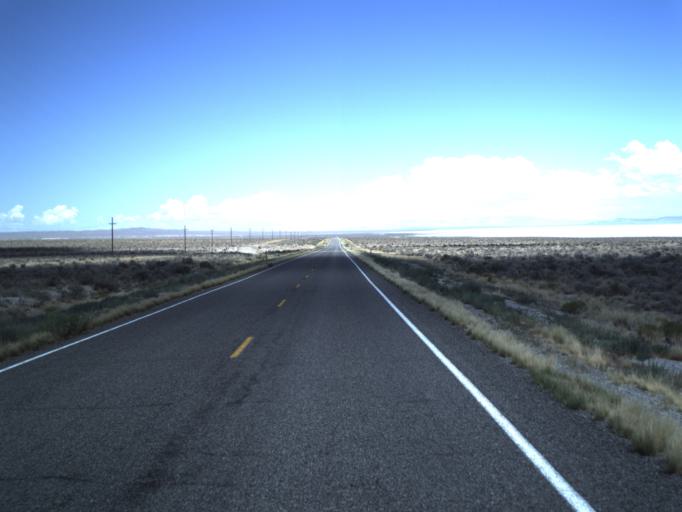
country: US
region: Utah
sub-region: Beaver County
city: Milford
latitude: 39.0634
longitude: -113.2388
